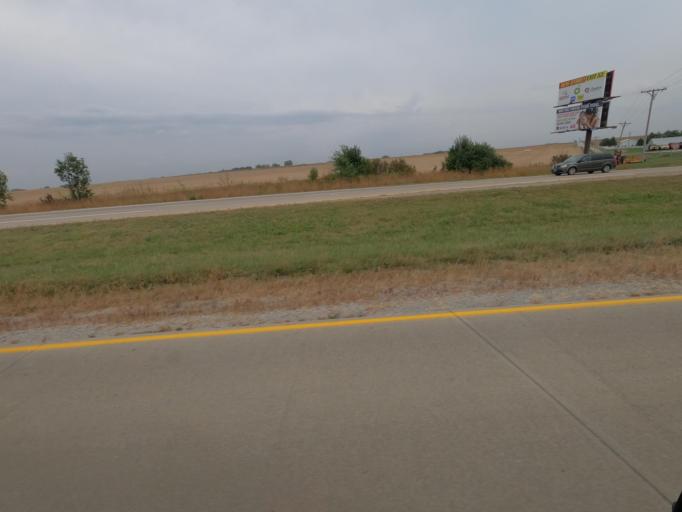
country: US
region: Iowa
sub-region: Marion County
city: Pella
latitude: 41.3792
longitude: -92.8187
